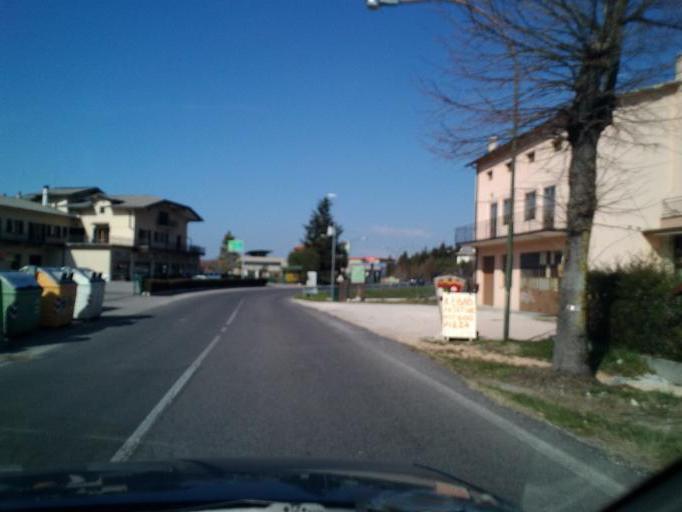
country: IT
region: Veneto
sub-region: Provincia di Verona
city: Cerro Veronese
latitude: 45.5721
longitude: 11.0426
